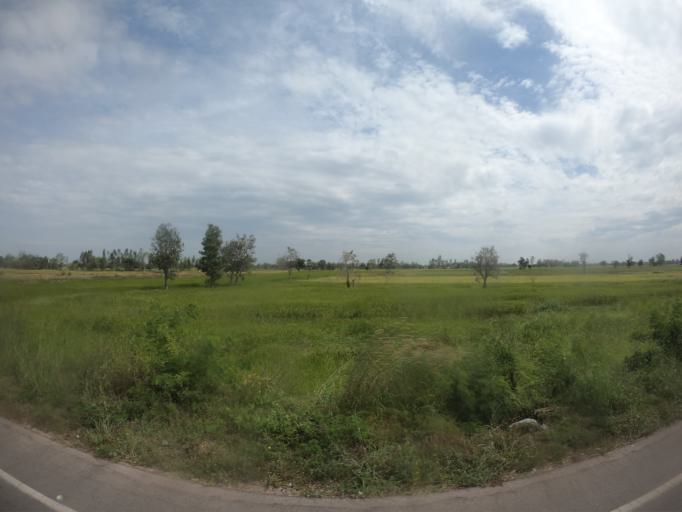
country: TH
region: Maha Sarakham
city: Chiang Yuen
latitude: 16.3754
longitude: 103.1048
